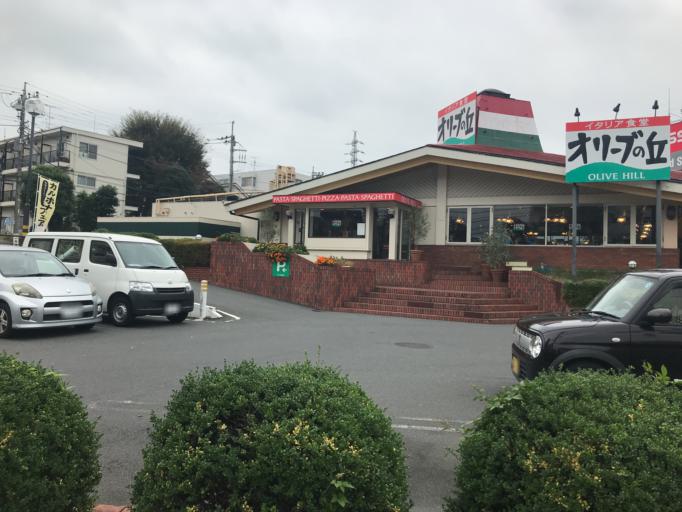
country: JP
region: Tokyo
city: Hino
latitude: 35.6349
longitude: 139.4462
